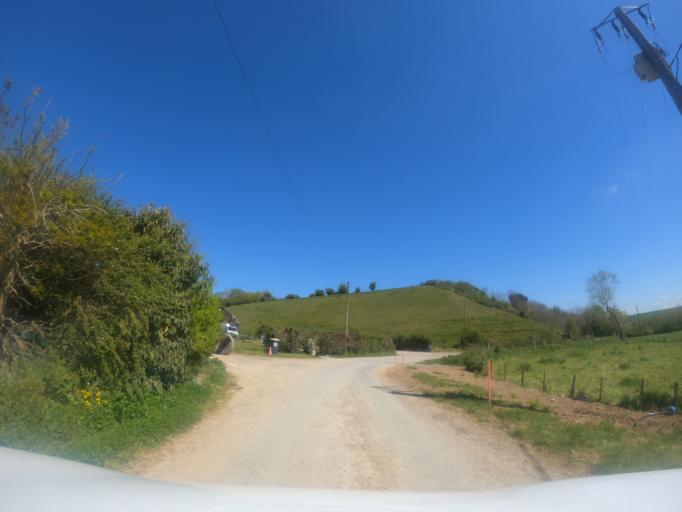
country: FR
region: Pays de la Loire
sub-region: Departement de la Vendee
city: Le Langon
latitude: 46.4355
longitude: -0.8848
